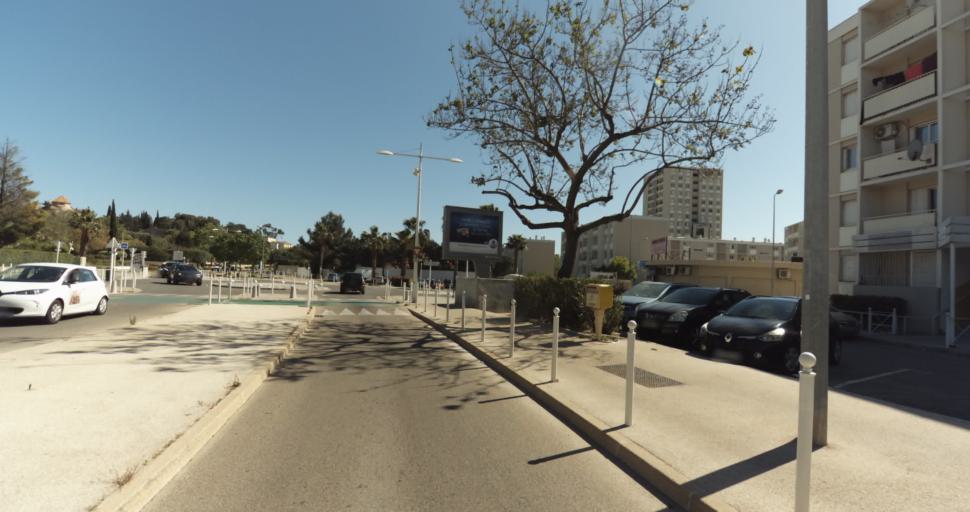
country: FR
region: Provence-Alpes-Cote d'Azur
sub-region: Departement du Var
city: La Valette-du-Var
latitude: 43.1260
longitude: 5.9813
